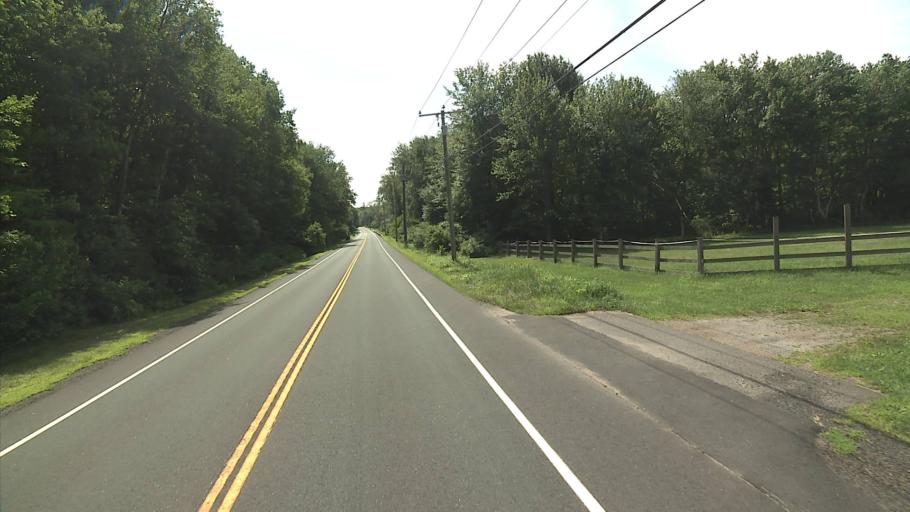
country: US
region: Connecticut
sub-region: Tolland County
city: Tolland
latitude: 41.8347
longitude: -72.4041
